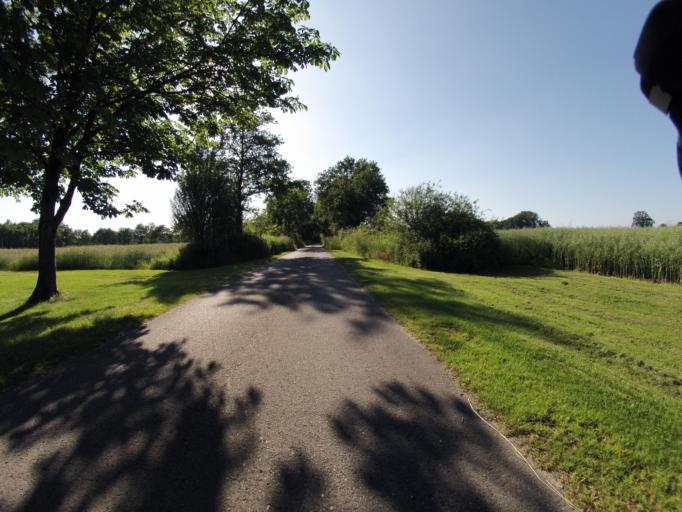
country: DE
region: Lower Saxony
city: Ohne
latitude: 52.3063
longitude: 7.3078
